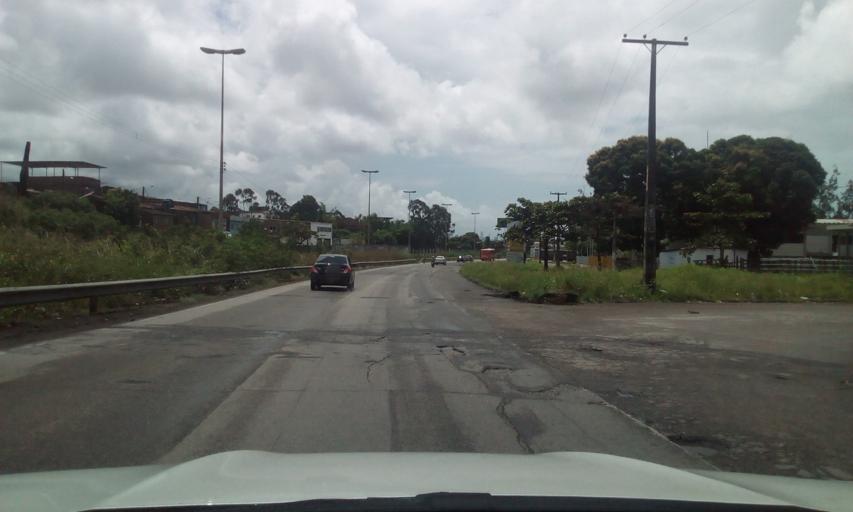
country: BR
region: Pernambuco
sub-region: Jaboatao Dos Guararapes
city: Jaboatao dos Guararapes
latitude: -8.0872
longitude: -34.9465
